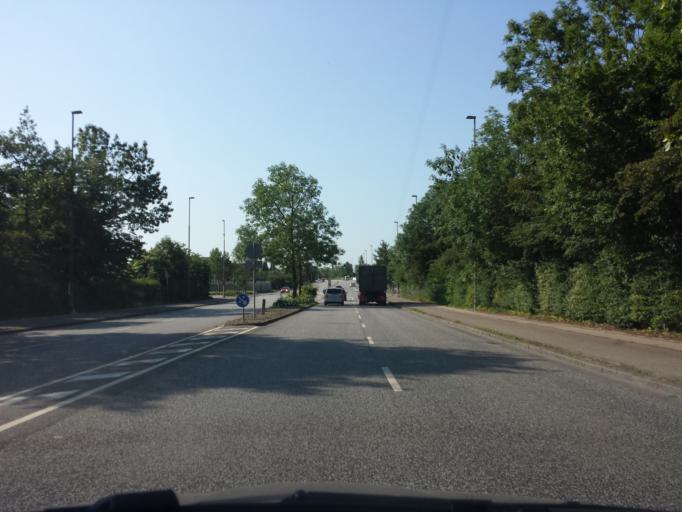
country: DK
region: Capital Region
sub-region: Ballerup Kommune
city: Ballerup
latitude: 55.7251
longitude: 12.3460
